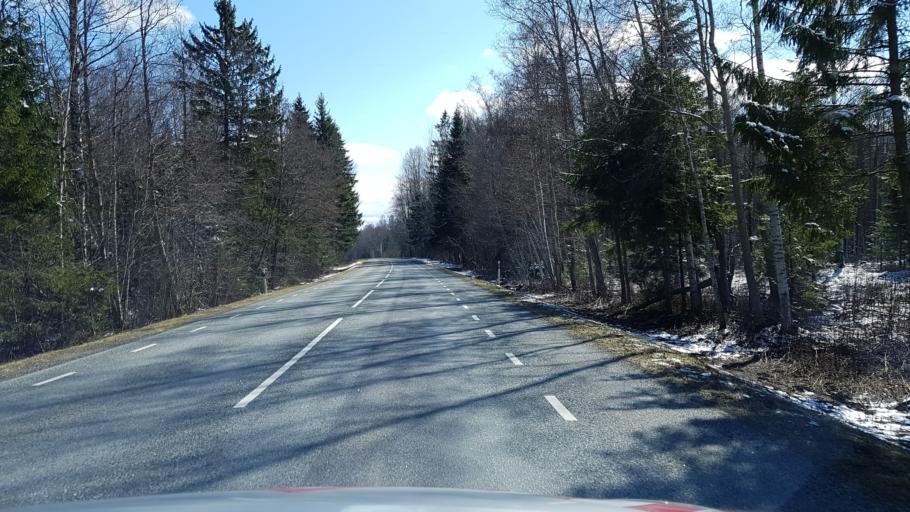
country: EE
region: Laeaene-Virumaa
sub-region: Tapa vald
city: Tapa
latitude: 59.4379
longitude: 25.9601
